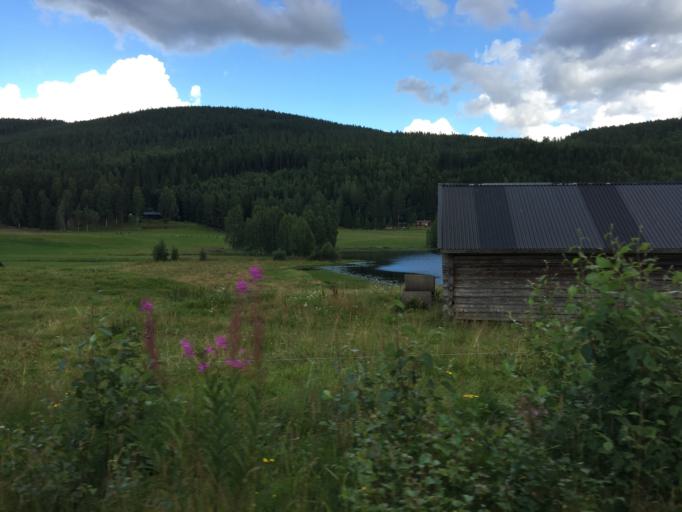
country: SE
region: Gaevleborg
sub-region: Ljusdals Kommun
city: Jaervsoe
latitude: 61.7428
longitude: 16.2725
